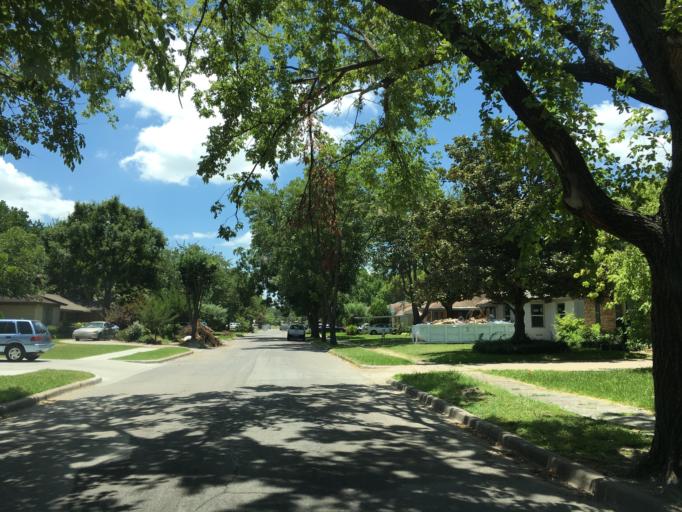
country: US
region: Texas
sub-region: Dallas County
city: Garland
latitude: 32.8493
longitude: -96.6688
